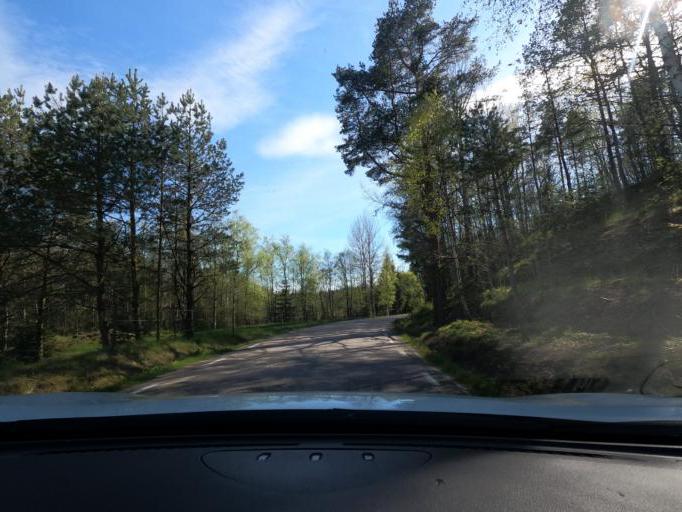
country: SE
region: Vaestra Goetaland
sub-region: Harryda Kommun
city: Hindas
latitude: 57.6394
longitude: 12.3402
